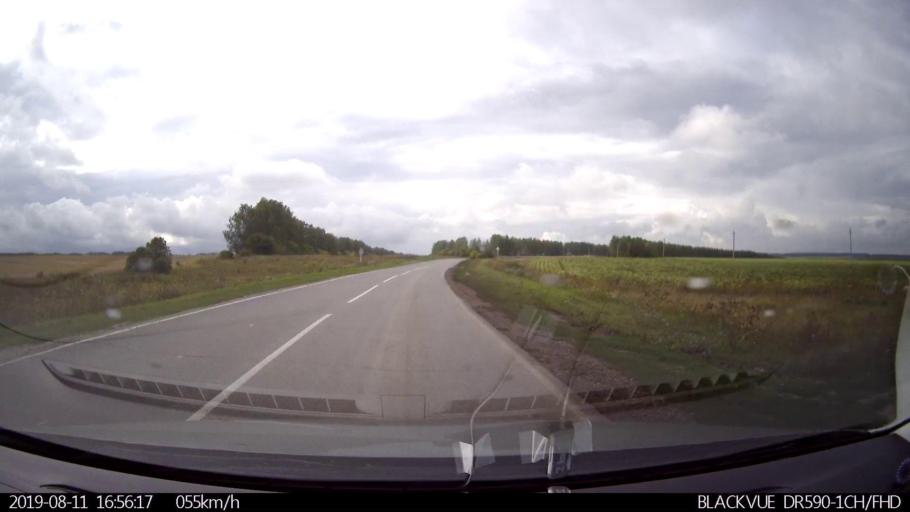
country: RU
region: Ulyanovsk
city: Mayna
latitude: 54.2867
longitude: 47.6551
